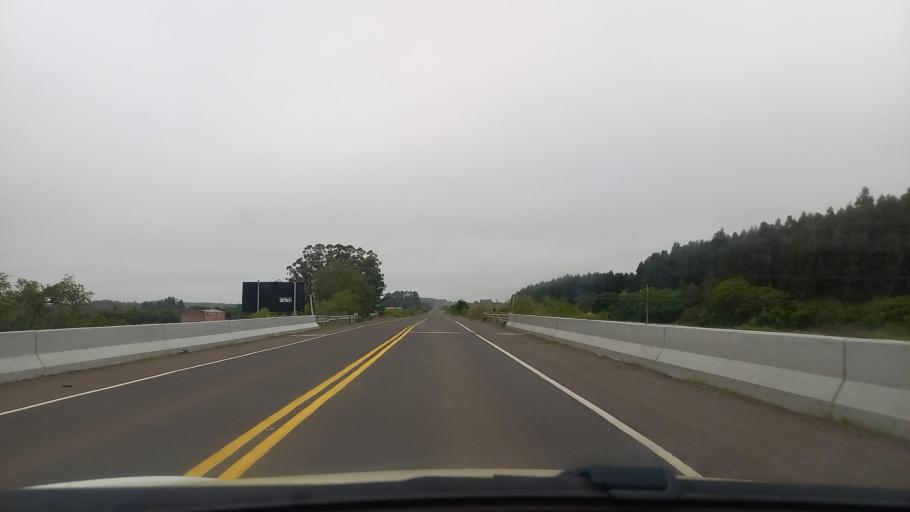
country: BR
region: Rio Grande do Sul
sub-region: Rosario Do Sul
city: Rosario do Sul
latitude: -30.2949
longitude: -54.9882
